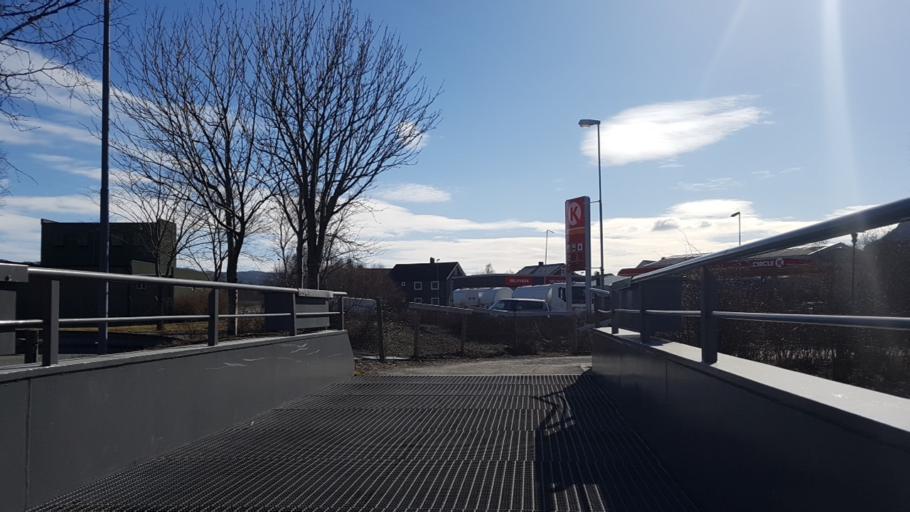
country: NO
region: Nordland
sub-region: Vefsn
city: Mosjoen
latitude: 65.8425
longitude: 13.2011
